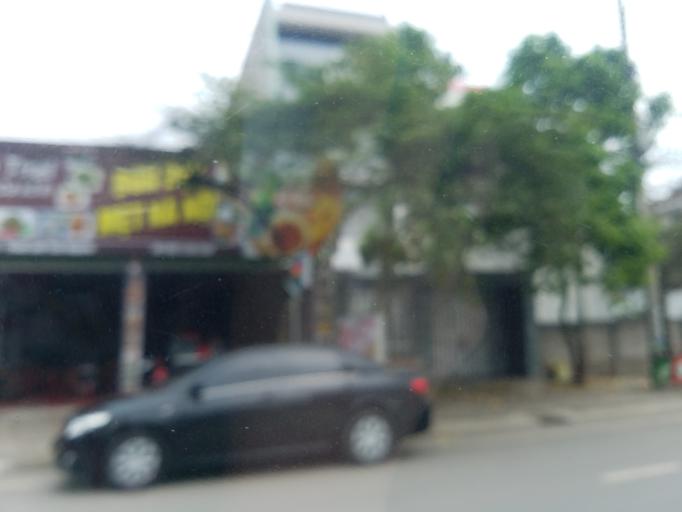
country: VN
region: Thai Nguyen
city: Thanh Pho Thai Nguyen
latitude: 21.5794
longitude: 105.8348
